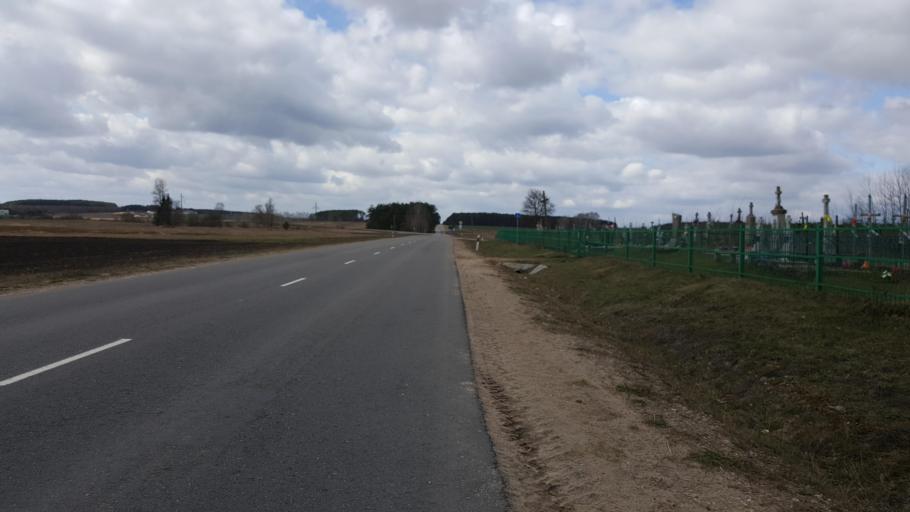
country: BY
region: Brest
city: Kamyanyets
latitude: 52.3920
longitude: 23.7582
